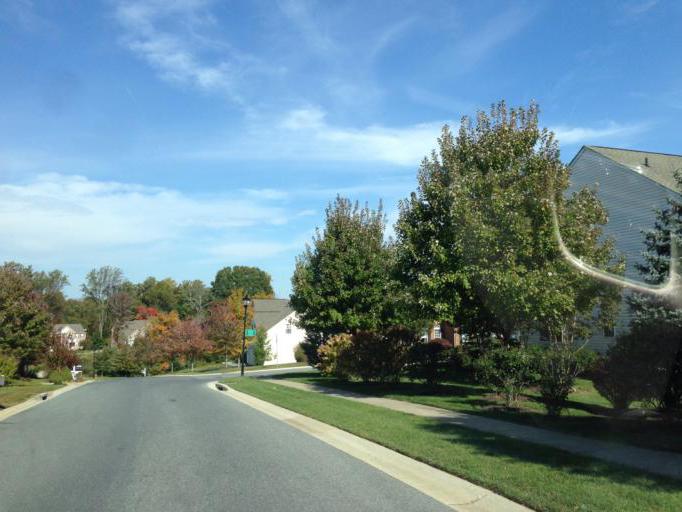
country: US
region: Maryland
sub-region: Howard County
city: Ellicott City
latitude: 39.2493
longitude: -76.8021
